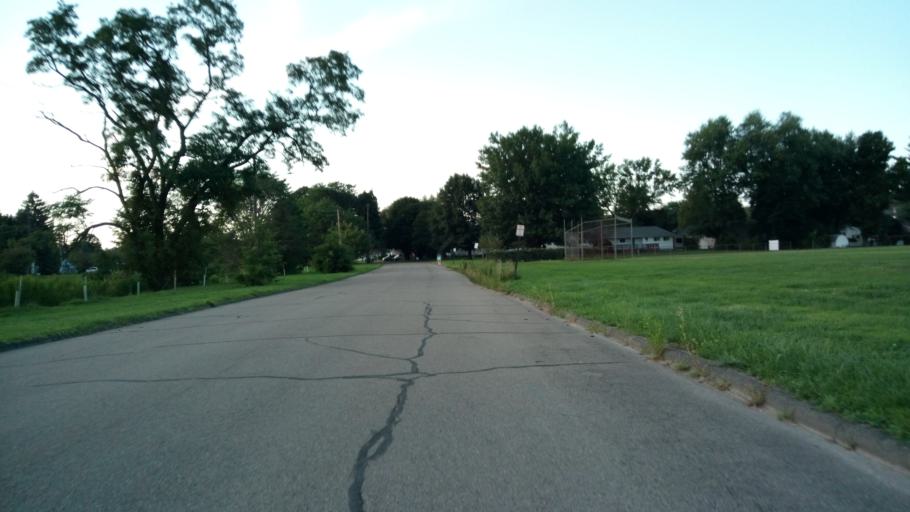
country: US
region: New York
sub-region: Chemung County
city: Elmira
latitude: 42.0728
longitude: -76.7914
